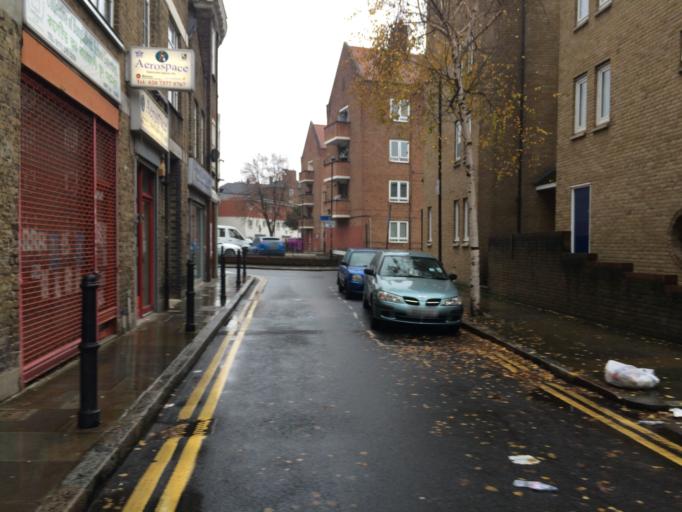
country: GB
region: England
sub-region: Greater London
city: Bethnal Green
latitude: 51.5198
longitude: -0.0699
